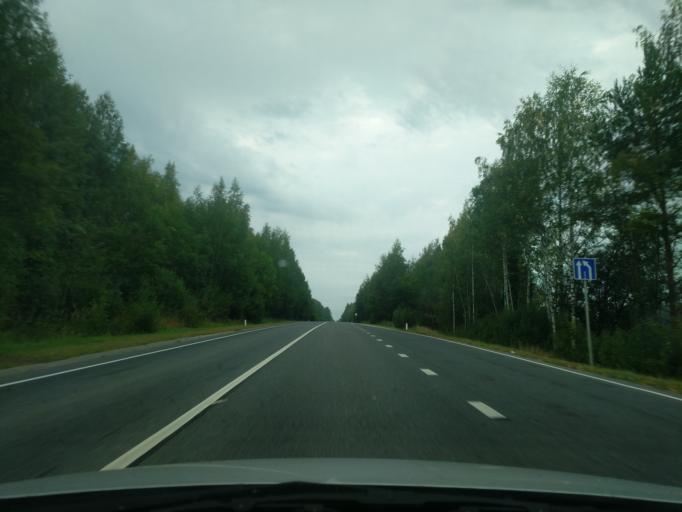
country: RU
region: Kirov
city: Torfyanoy
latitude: 58.7068
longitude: 49.1906
